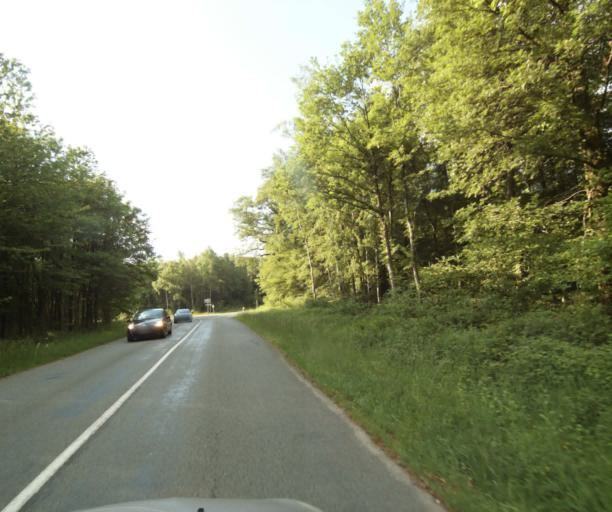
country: FR
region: Champagne-Ardenne
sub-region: Departement des Ardennes
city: Warcq
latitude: 49.8195
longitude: 4.6990
